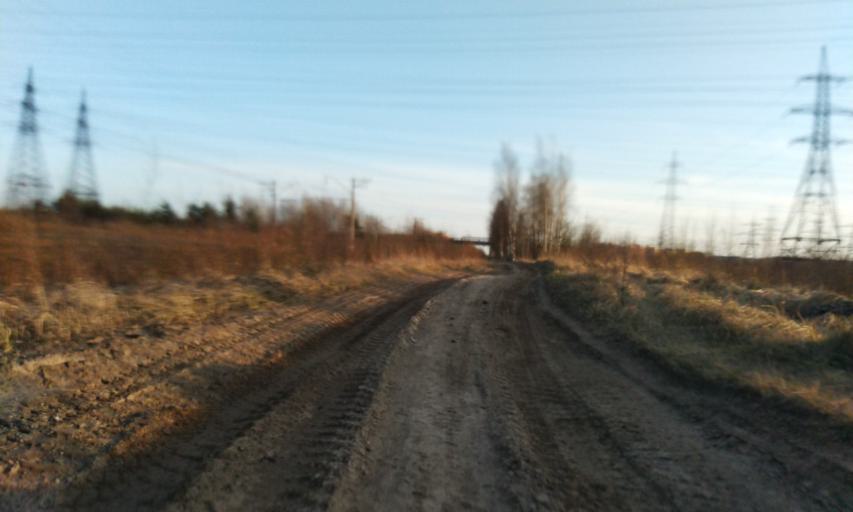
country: RU
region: Leningrad
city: Novoye Devyatkino
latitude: 60.0816
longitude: 30.4630
